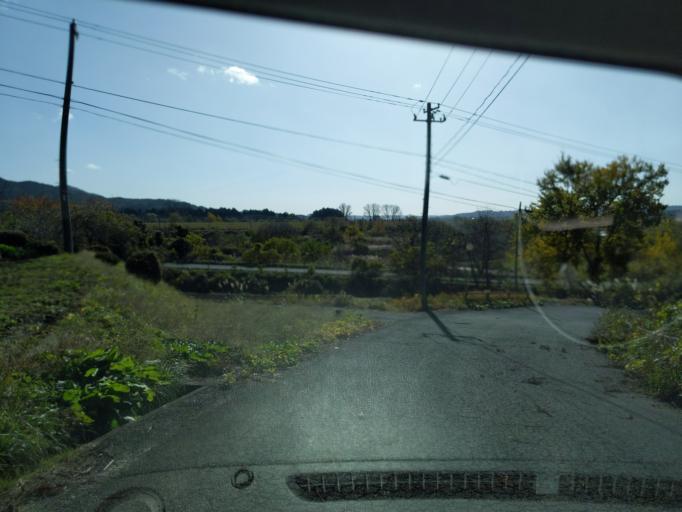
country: JP
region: Iwate
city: Ichinoseki
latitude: 39.0214
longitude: 141.1262
